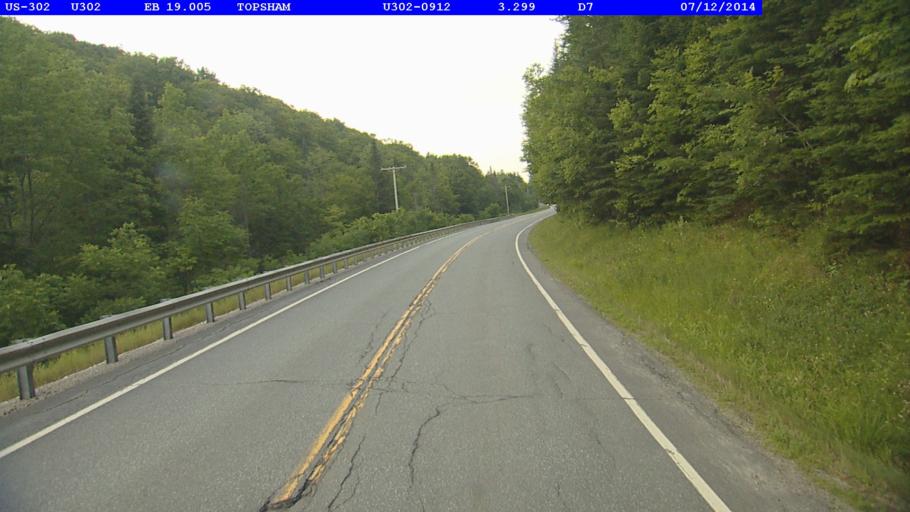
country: US
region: Vermont
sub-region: Washington County
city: Barre
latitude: 44.1823
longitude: -72.2986
